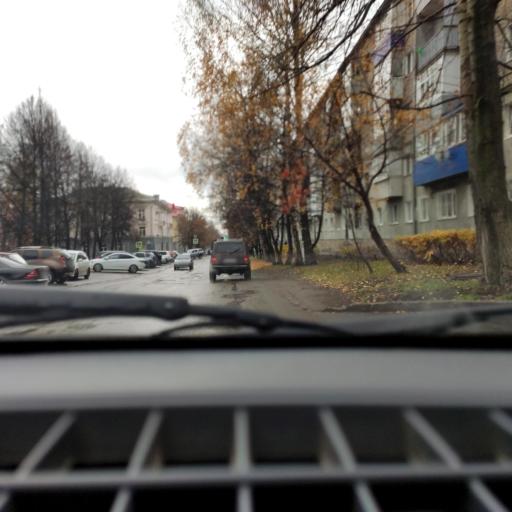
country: RU
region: Bashkortostan
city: Ufa
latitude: 54.8180
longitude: 56.0811
